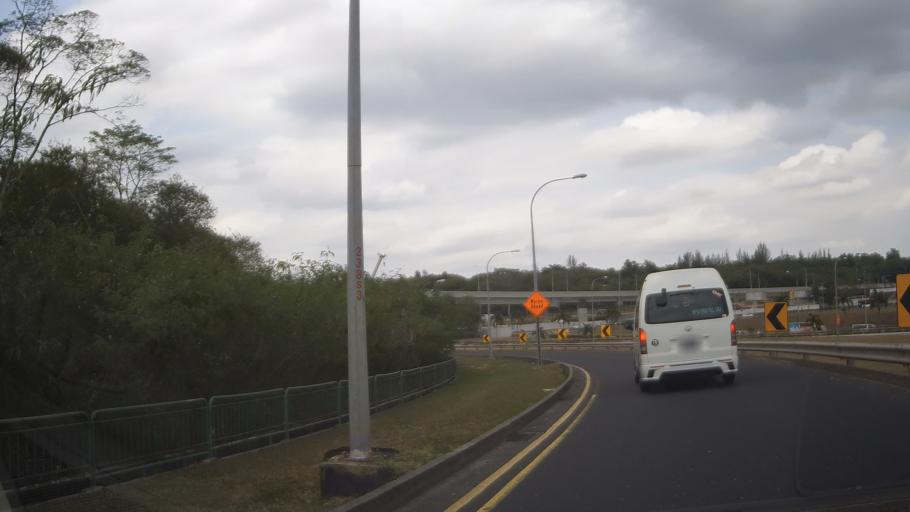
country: MY
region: Johor
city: Kampung Pasir Gudang Baru
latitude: 1.3815
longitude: 103.9164
